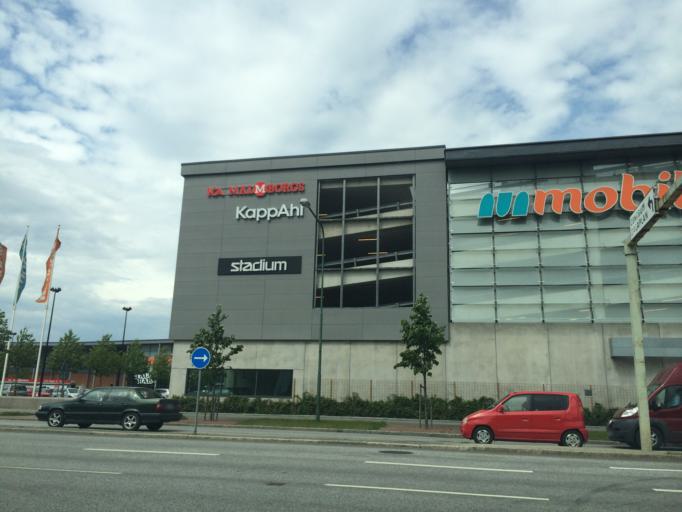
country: SE
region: Skane
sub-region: Malmo
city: Malmoe
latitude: 55.5788
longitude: 13.0042
